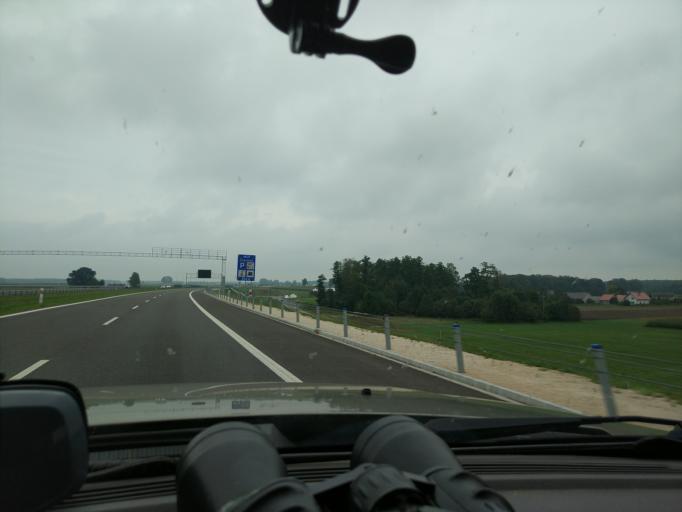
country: PL
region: Podlasie
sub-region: Powiat zambrowski
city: Szumowo
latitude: 52.9446
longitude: 22.1551
